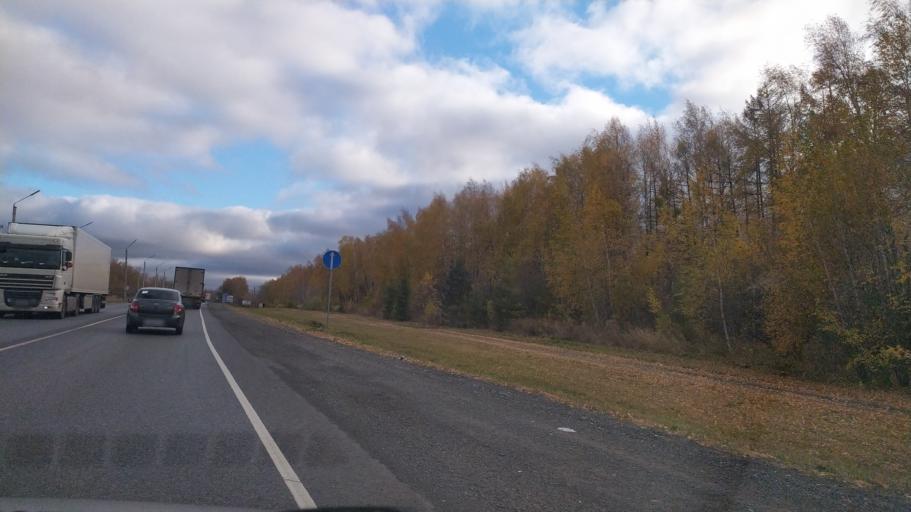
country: RU
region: Chuvashia
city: Kugesi
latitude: 56.0502
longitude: 47.2830
